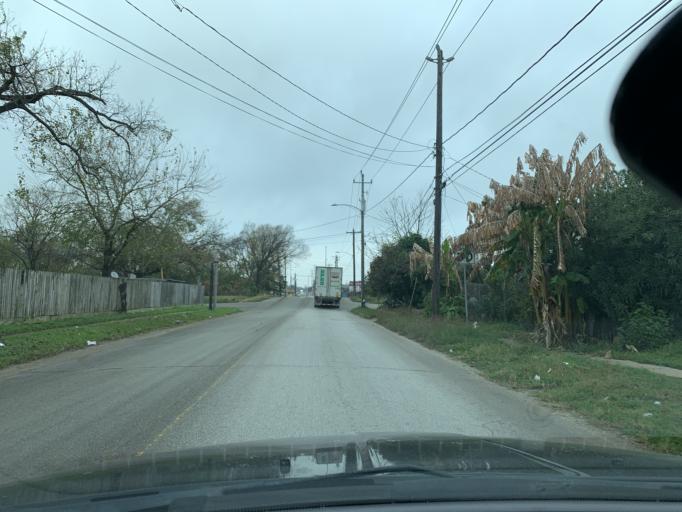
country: US
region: Texas
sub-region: Harris County
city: Houston
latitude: 29.7835
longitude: -95.3444
